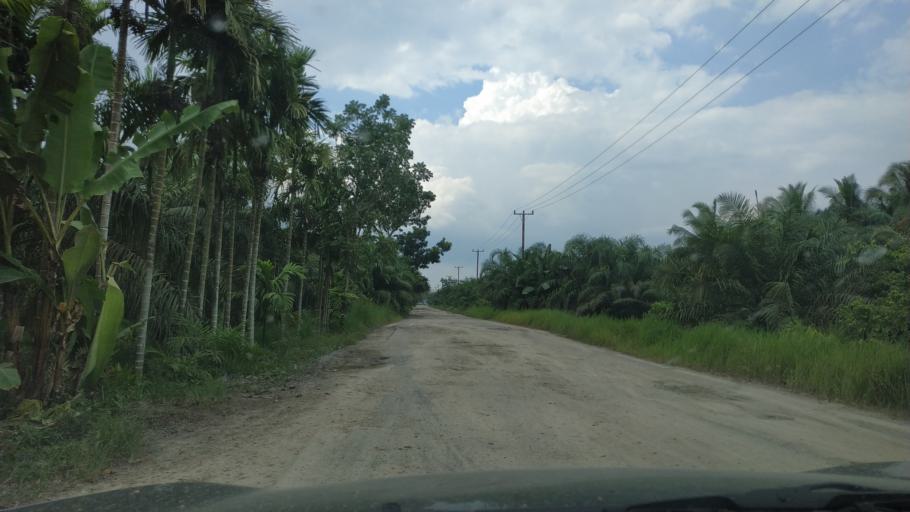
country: ID
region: Riau
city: Sungaisalak
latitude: -0.5240
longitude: 103.0041
